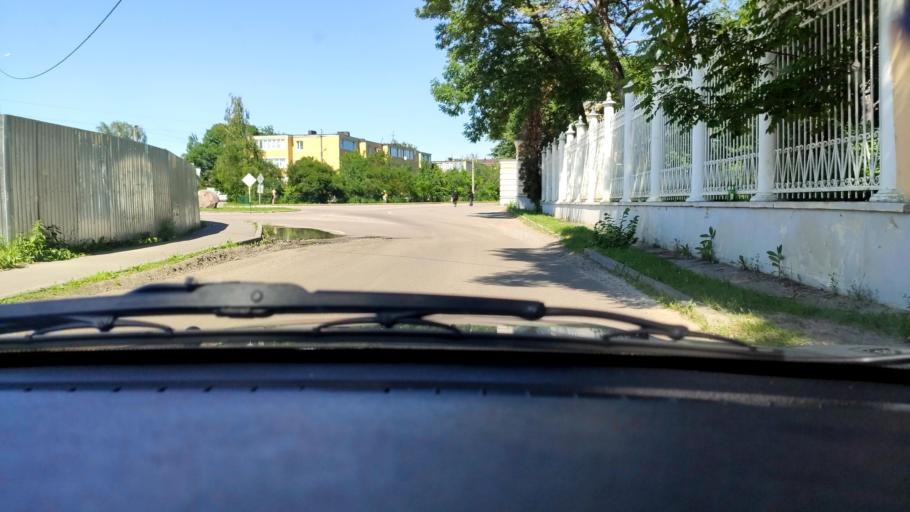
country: RU
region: Voronezj
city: Ramon'
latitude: 51.8248
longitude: 39.2619
